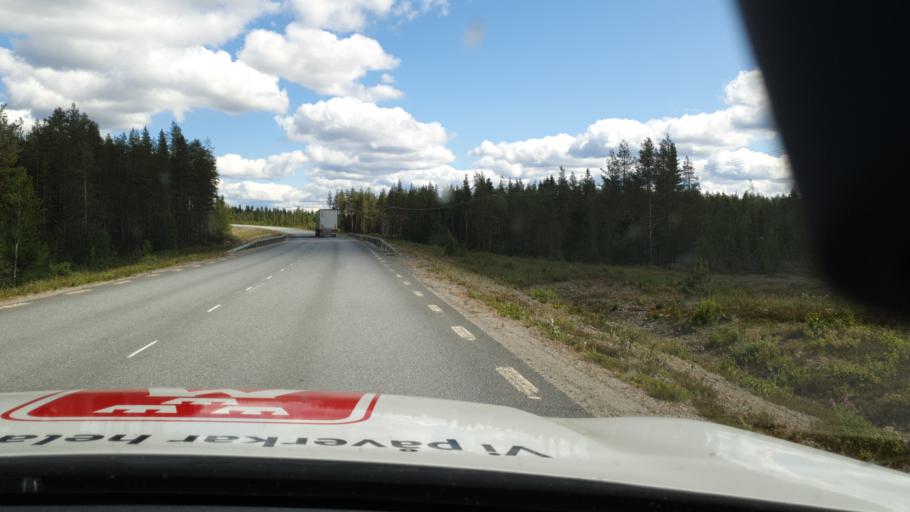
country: SE
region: Vaesterbotten
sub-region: Sorsele Kommun
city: Sorsele
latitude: 65.5574
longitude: 17.7553
